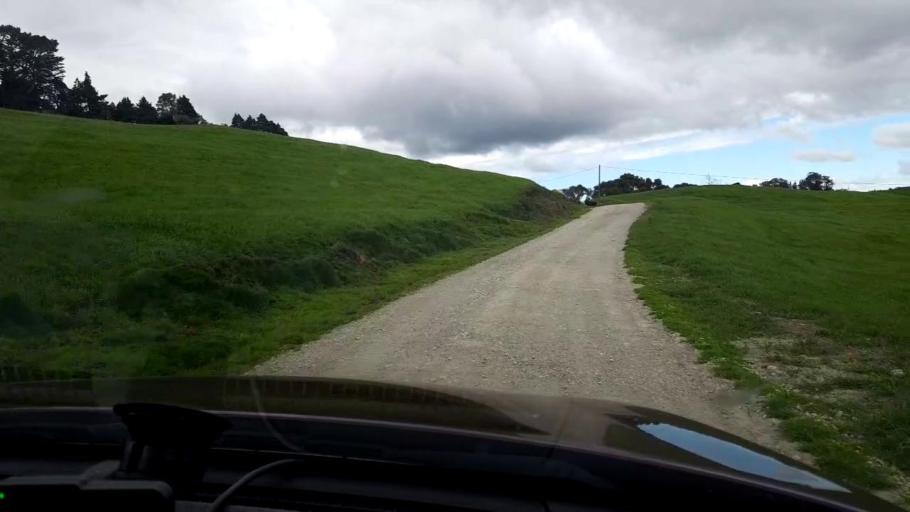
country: NZ
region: Gisborne
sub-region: Gisborne District
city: Gisborne
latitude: -38.3679
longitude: 177.9666
